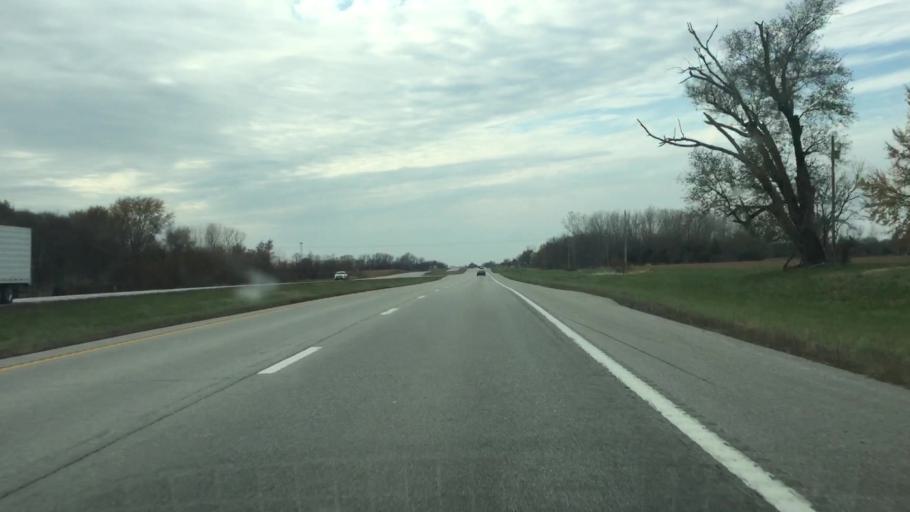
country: US
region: Missouri
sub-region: Cass County
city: Harrisonville
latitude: 38.6049
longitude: -94.2811
